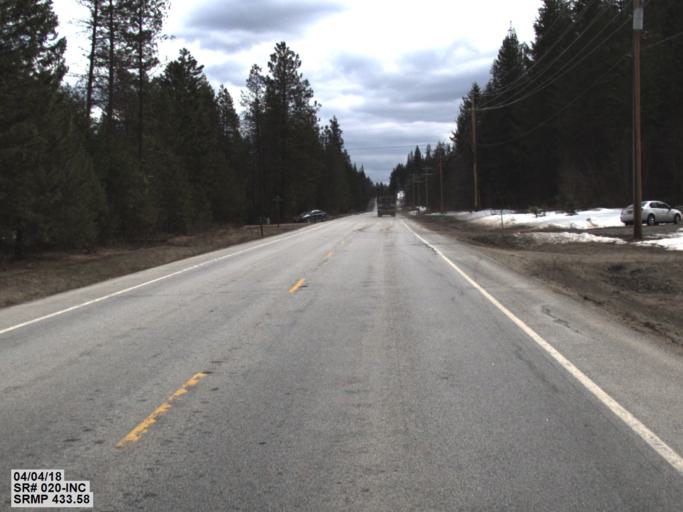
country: US
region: Washington
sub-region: Pend Oreille County
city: Newport
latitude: 48.2177
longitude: -117.0868
